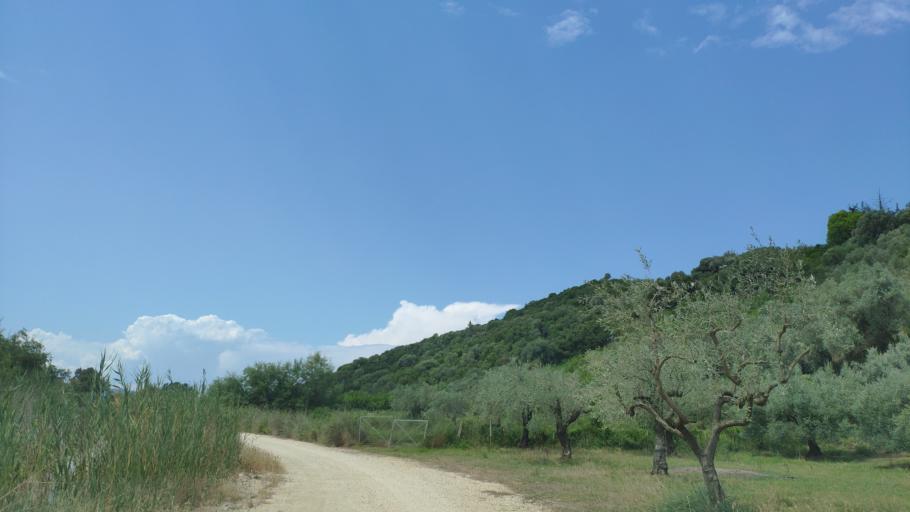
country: GR
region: West Greece
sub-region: Nomos Aitolias kai Akarnanias
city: Menidi
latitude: 39.0503
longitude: 21.1048
